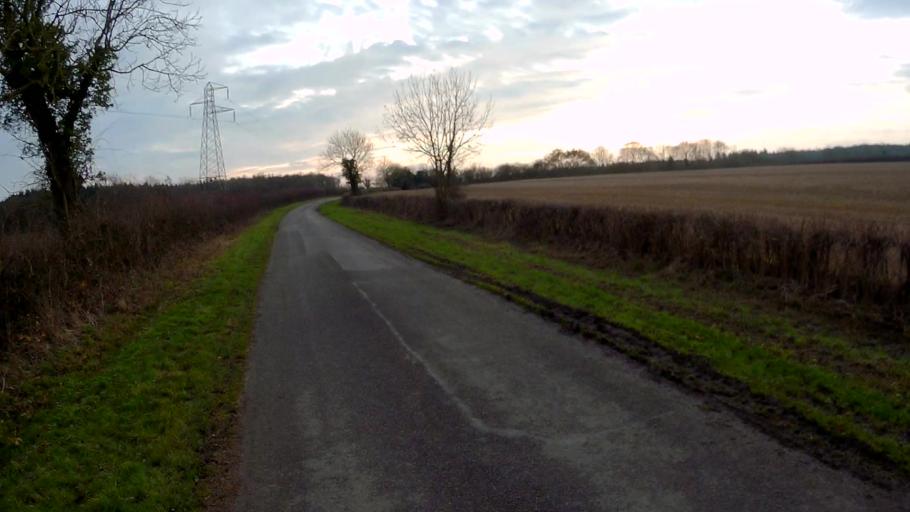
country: GB
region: England
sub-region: Lincolnshire
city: Bourne
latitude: 52.8250
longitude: -0.4056
